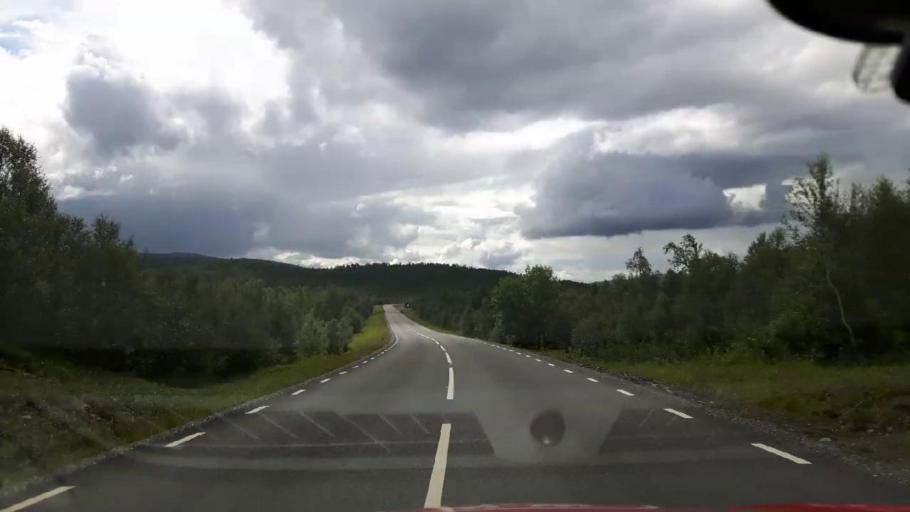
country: NO
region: Nordland
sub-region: Hattfjelldal
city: Hattfjelldal
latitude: 64.9833
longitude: 14.2128
